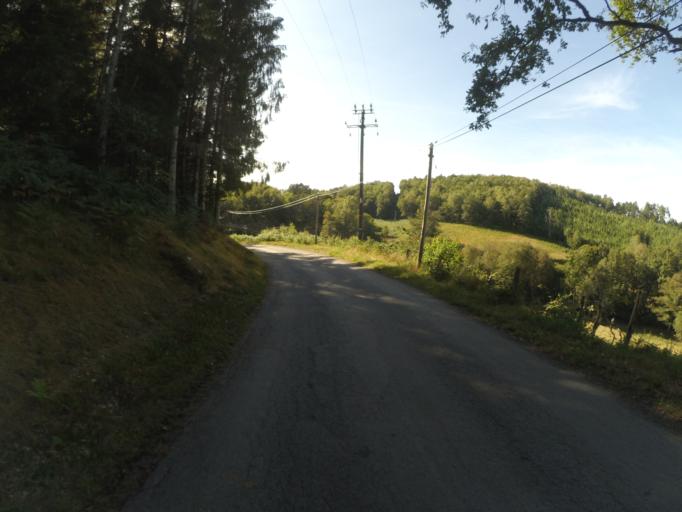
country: FR
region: Limousin
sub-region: Departement de la Correze
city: Bugeat
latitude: 45.6862
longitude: 1.9366
